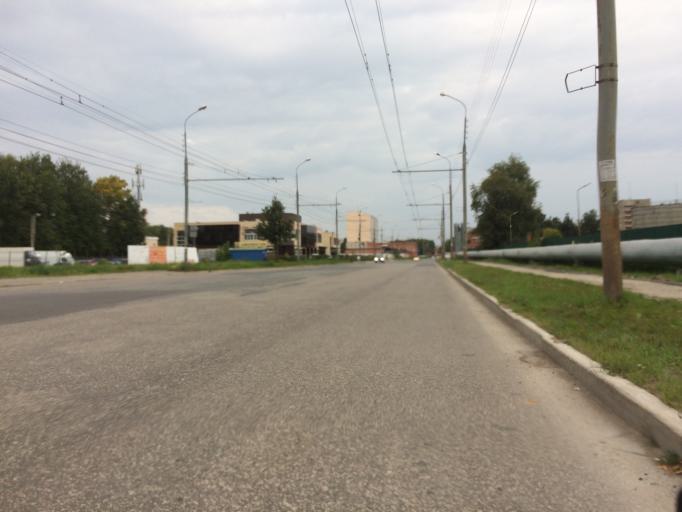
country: RU
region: Mariy-El
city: Yoshkar-Ola
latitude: 56.6313
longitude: 47.8714
